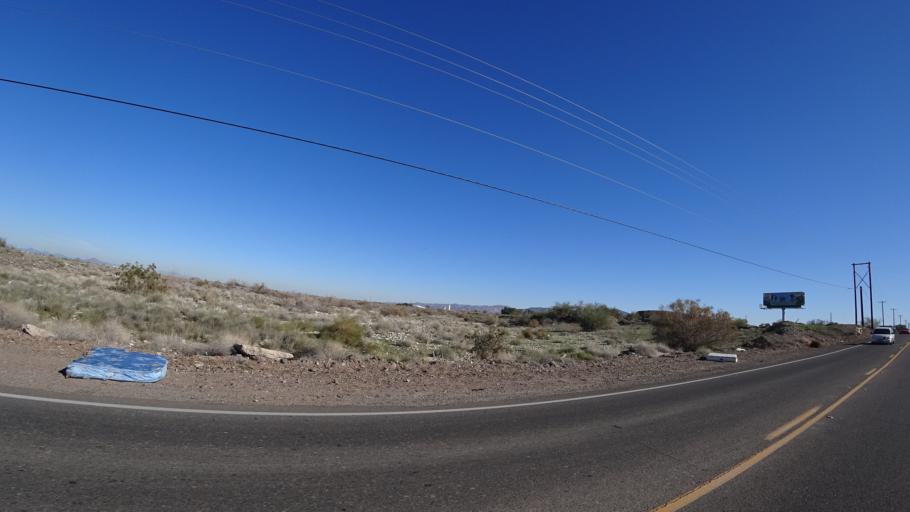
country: US
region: Arizona
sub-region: Maricopa County
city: Laveen
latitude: 33.3959
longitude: -112.2033
